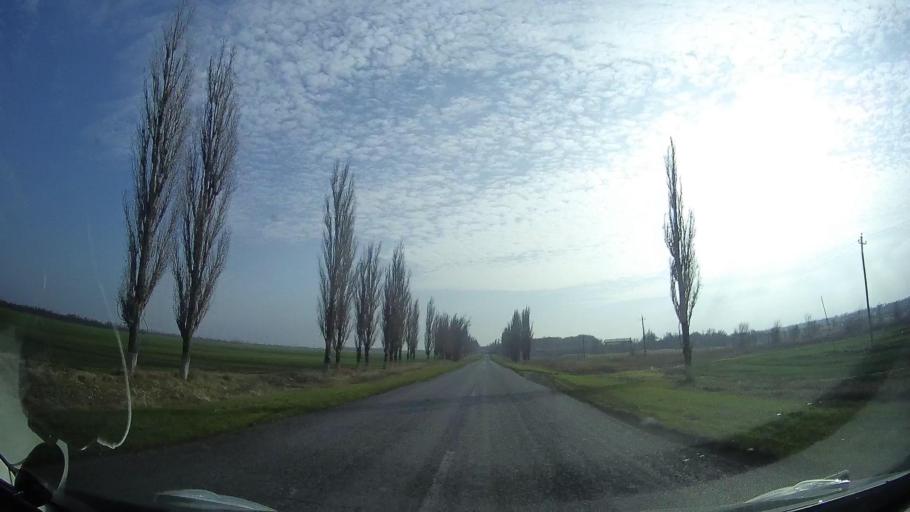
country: RU
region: Rostov
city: Mechetinskaya
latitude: 46.8316
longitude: 40.5505
